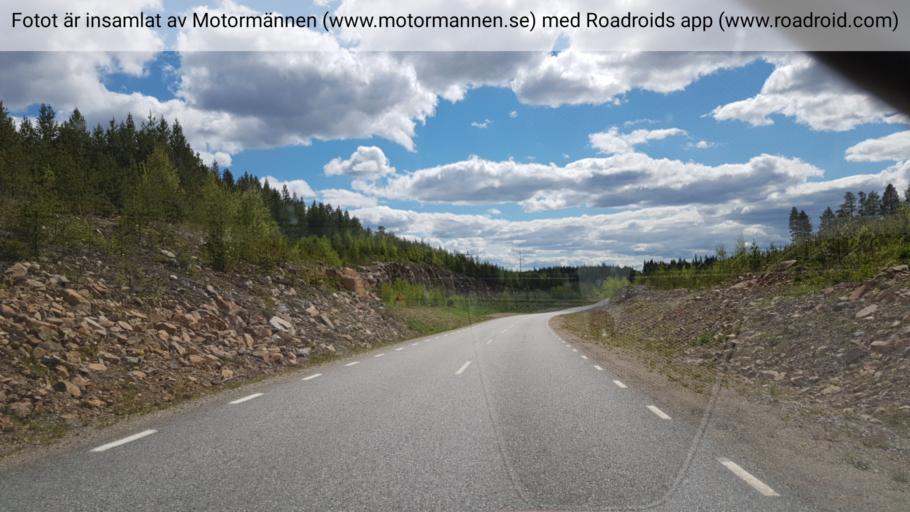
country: SE
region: Vaesterbotten
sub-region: Skelleftea Kommun
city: Langsele
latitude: 64.7440
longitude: 19.9509
